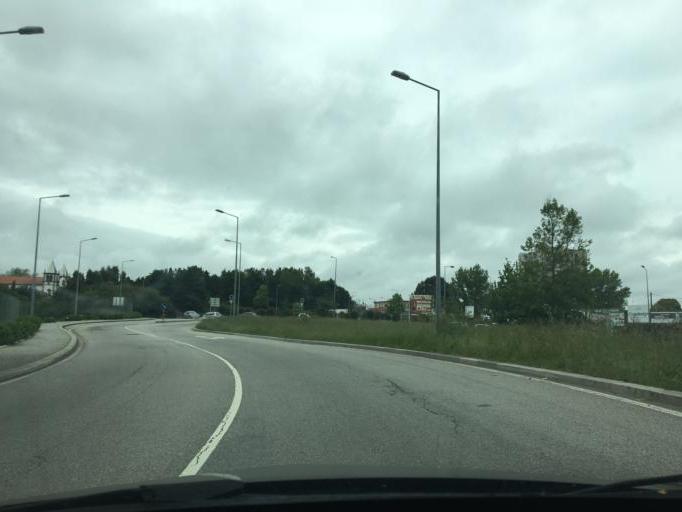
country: PT
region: Porto
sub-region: Maia
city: Gemunde
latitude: 41.2424
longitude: -8.6485
